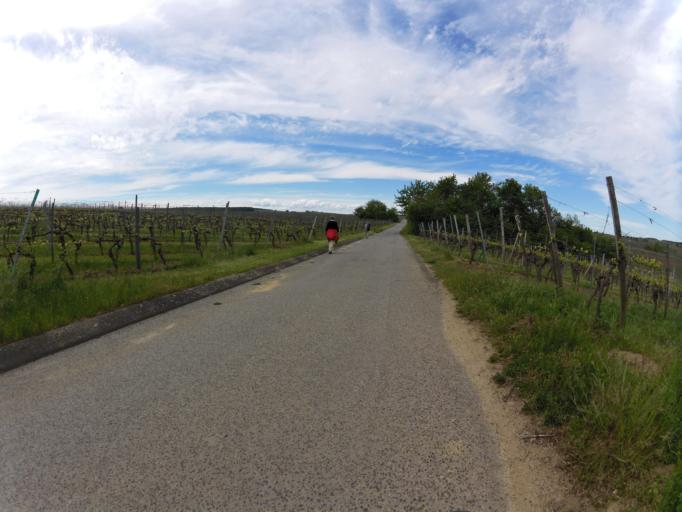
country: DE
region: Bavaria
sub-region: Regierungsbezirk Unterfranken
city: Nordheim
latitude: 49.8525
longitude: 10.2018
